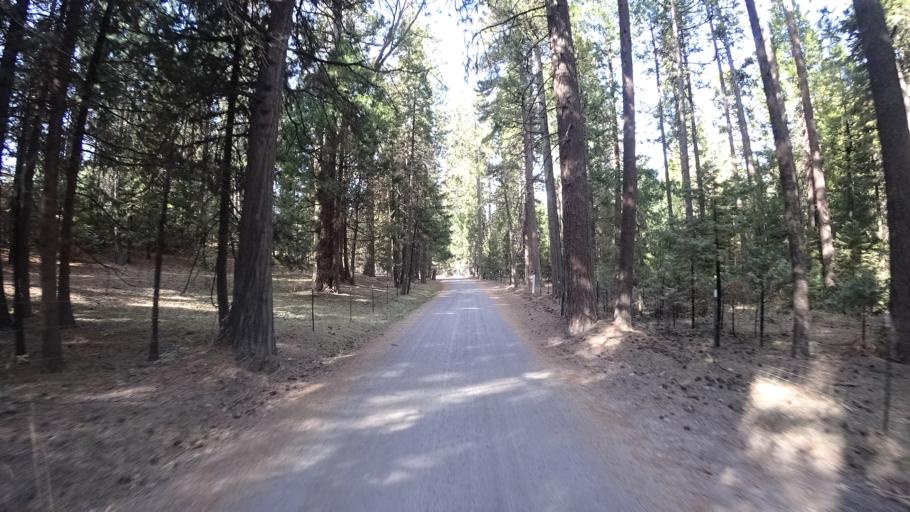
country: US
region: California
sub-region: Siskiyou County
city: Weed
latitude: 41.4341
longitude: -122.4135
